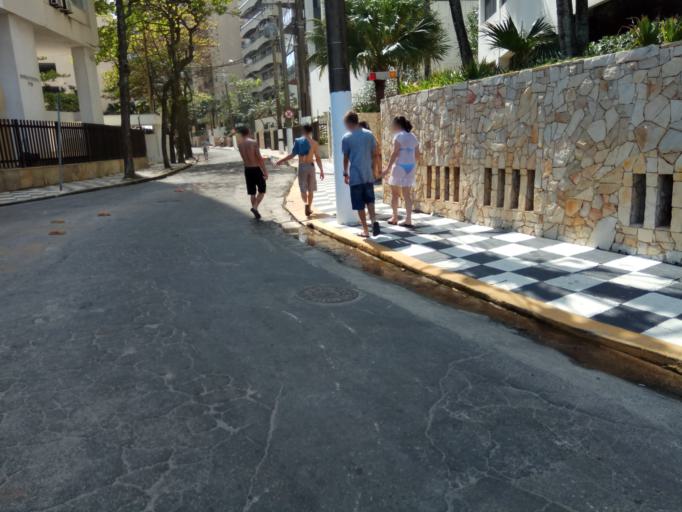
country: BR
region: Sao Paulo
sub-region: Guaruja
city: Guaruja
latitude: -23.9951
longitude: -46.2513
